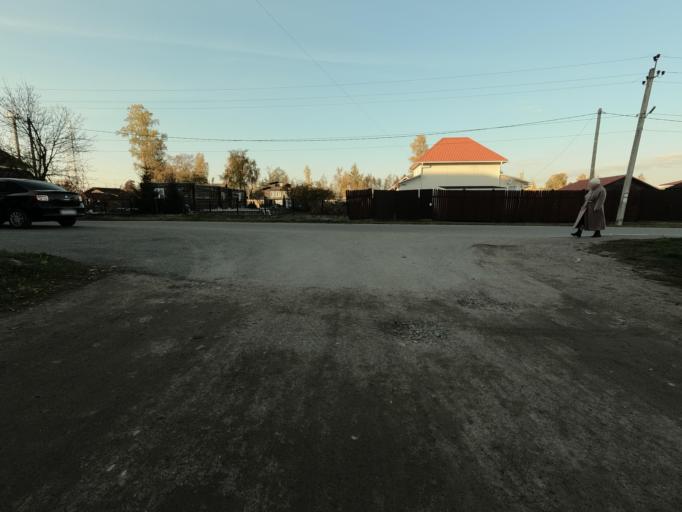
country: RU
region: Leningrad
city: Mga
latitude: 59.7606
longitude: 31.0654
